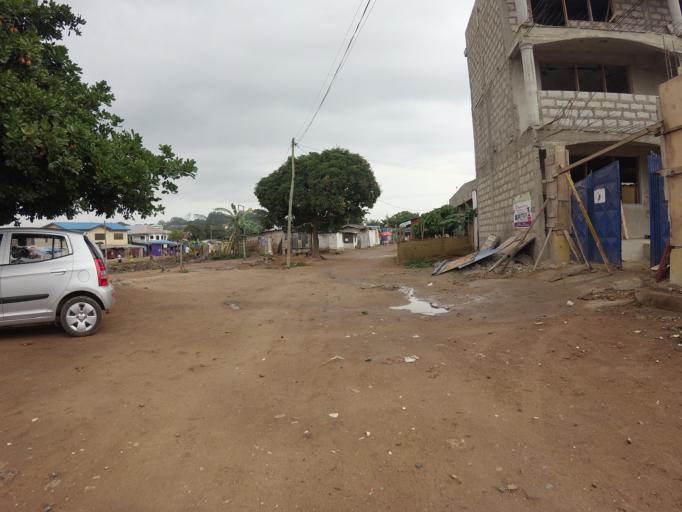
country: GH
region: Greater Accra
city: Dome
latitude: 5.6330
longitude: -0.2300
